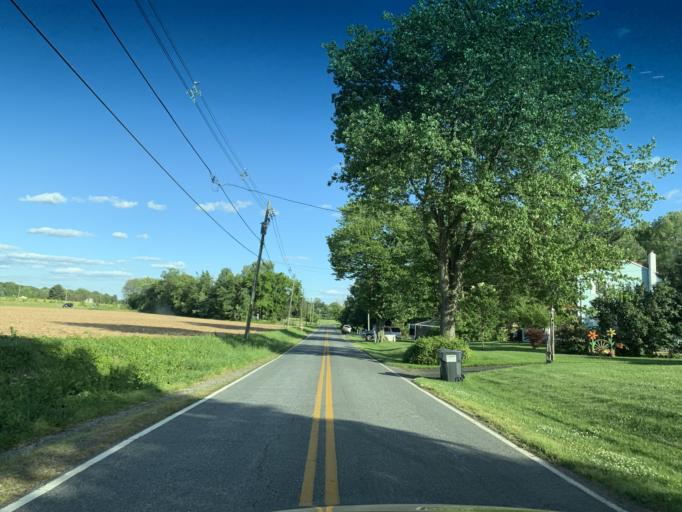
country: US
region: Maryland
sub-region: Cecil County
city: North East
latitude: 39.6751
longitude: -75.9644
